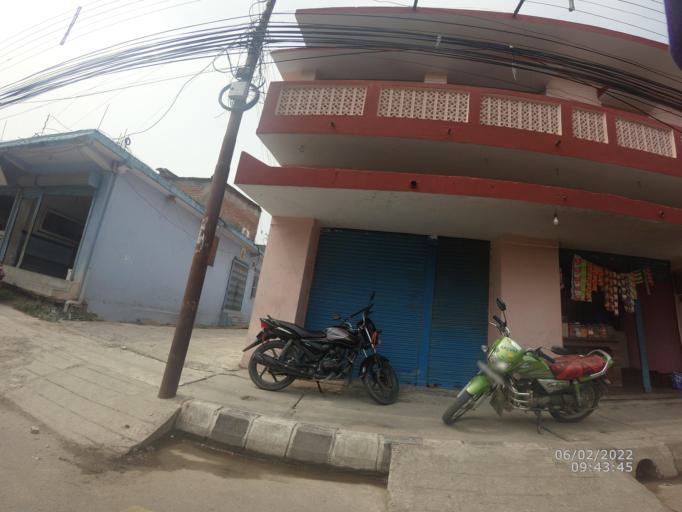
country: NP
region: Western Region
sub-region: Lumbini Zone
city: Bhairahawa
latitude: 27.5028
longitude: 83.4506
